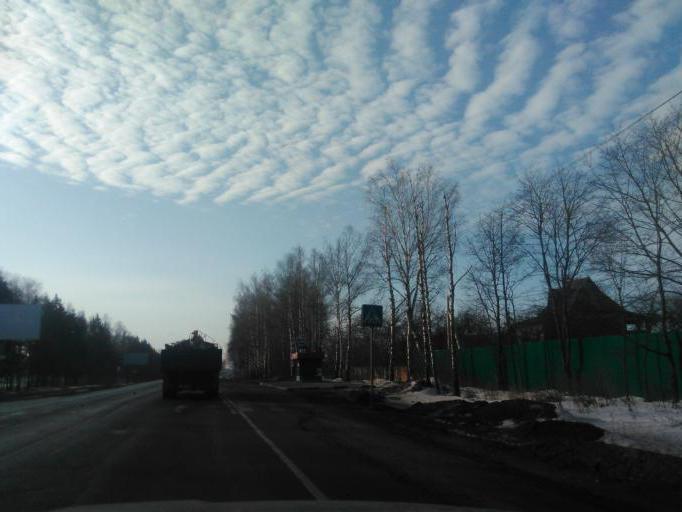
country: RU
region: Moskovskaya
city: Snegiri
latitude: 55.8802
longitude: 36.9437
